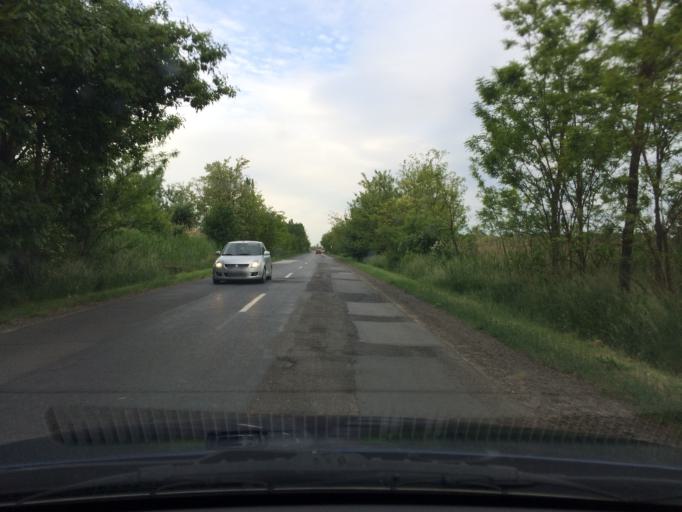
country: HU
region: Hajdu-Bihar
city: Hajdunanas
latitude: 47.8901
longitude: 21.4121
